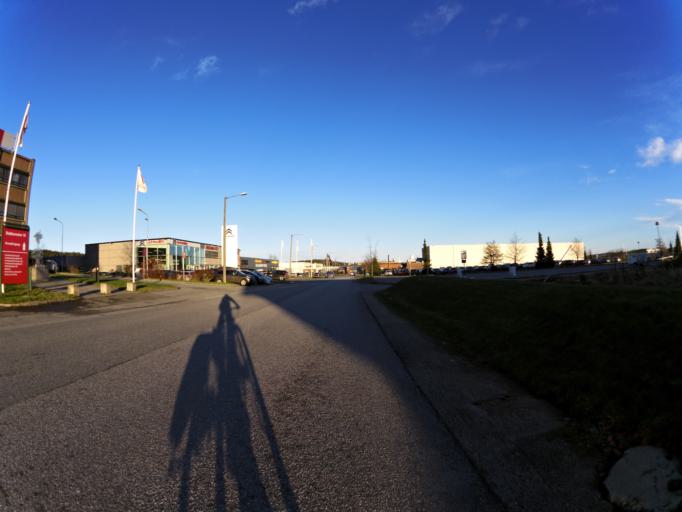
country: NO
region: Ostfold
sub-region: Fredrikstad
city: Fredrikstad
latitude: 59.2408
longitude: 10.9699
